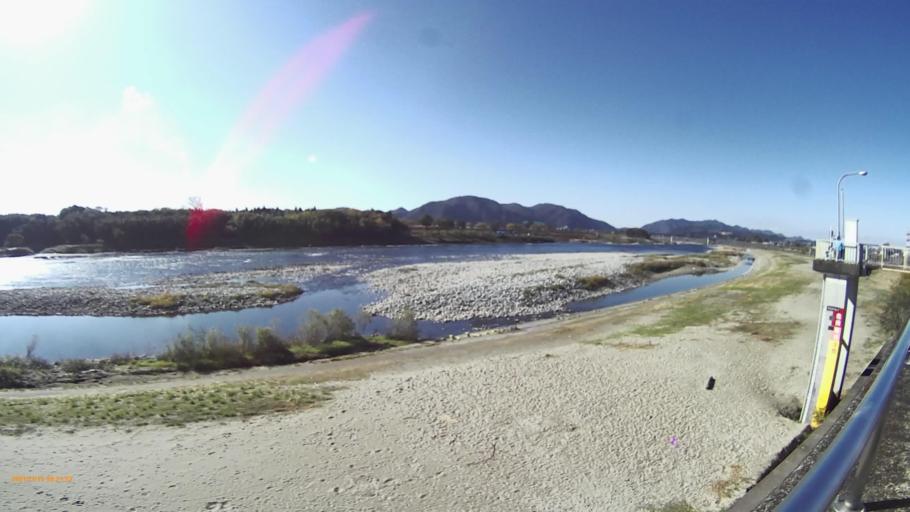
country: JP
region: Gifu
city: Minokamo
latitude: 35.4380
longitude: 137.0258
